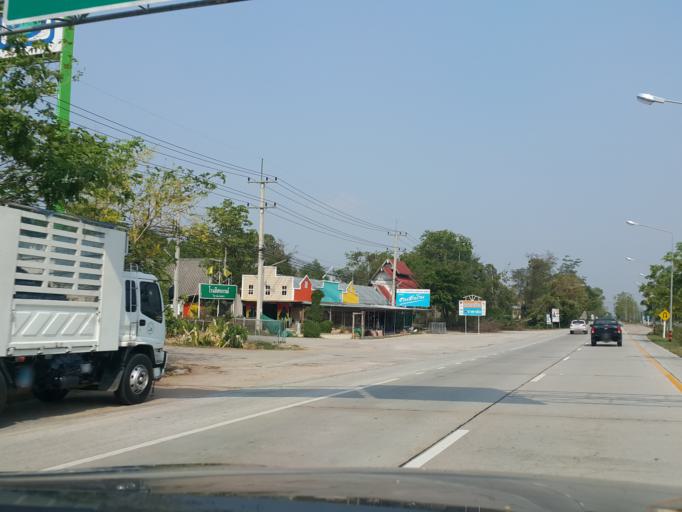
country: TH
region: Lampang
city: Hang Chat
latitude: 18.3105
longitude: 99.3896
